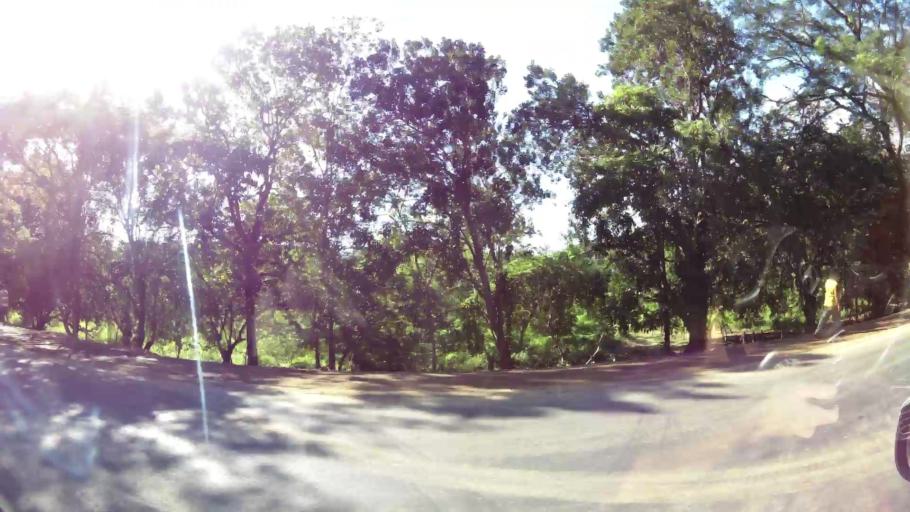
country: CR
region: Puntarenas
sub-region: Canton de Garabito
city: Jaco
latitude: 9.6019
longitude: -84.6160
